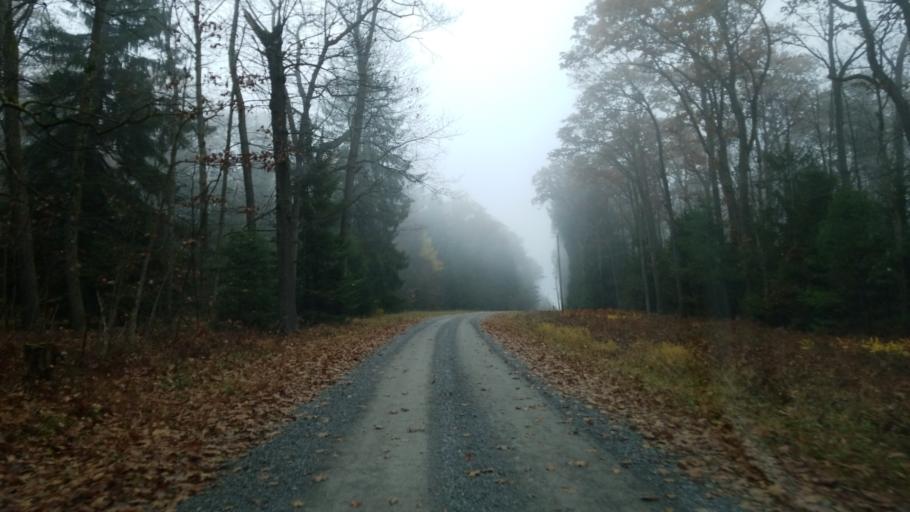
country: US
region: Pennsylvania
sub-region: Clearfield County
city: Clearfield
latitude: 41.1018
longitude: -78.5265
